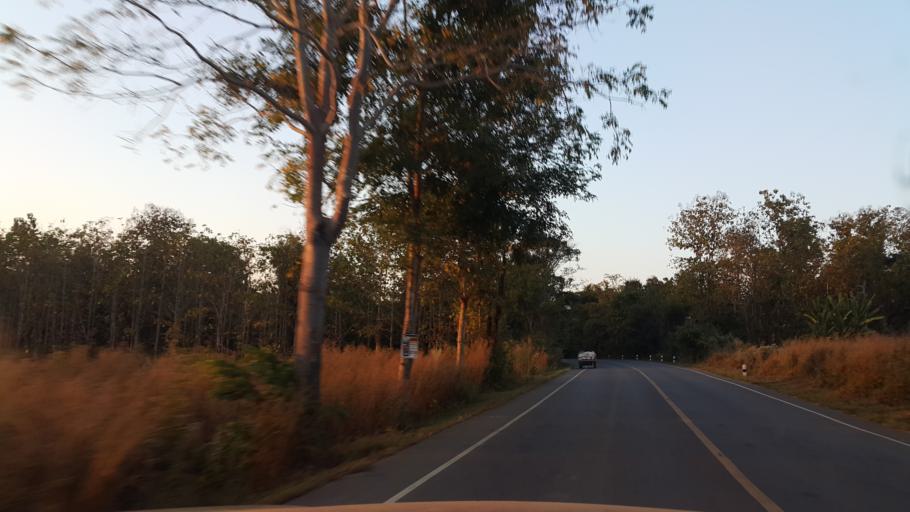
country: TH
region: Phrae
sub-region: Amphoe Wang Chin
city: Wang Chin
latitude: 17.8579
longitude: 99.6264
